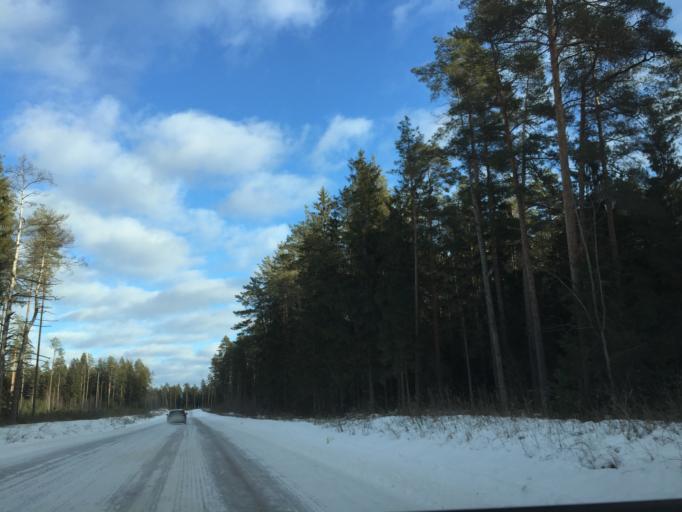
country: LV
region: Ogre
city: Jumprava
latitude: 56.5884
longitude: 24.9713
